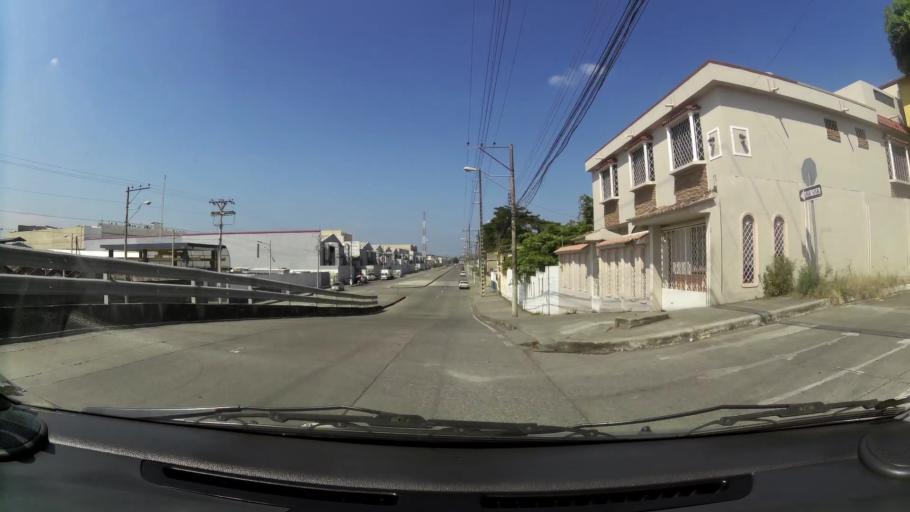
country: EC
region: Guayas
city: Eloy Alfaro
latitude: -2.1255
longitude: -79.9076
